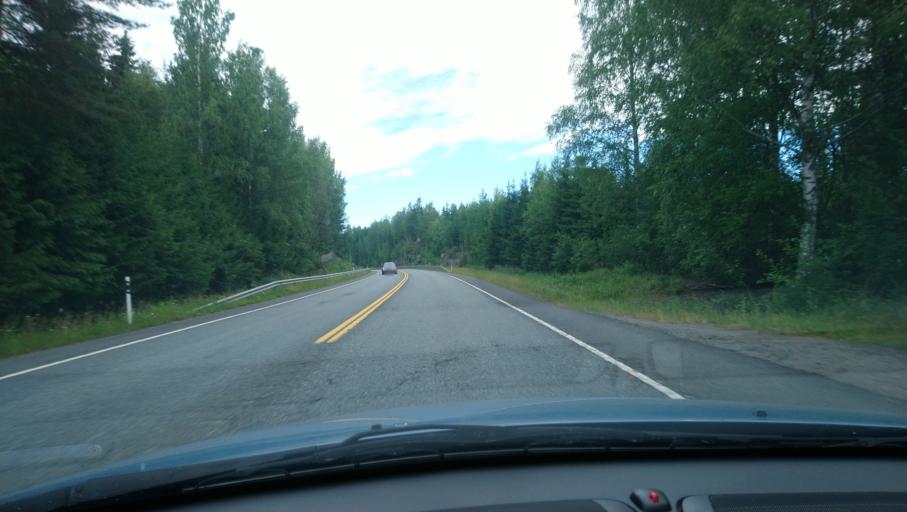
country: FI
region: Uusimaa
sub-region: Porvoo
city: Porvoo
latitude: 60.4236
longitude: 25.5798
